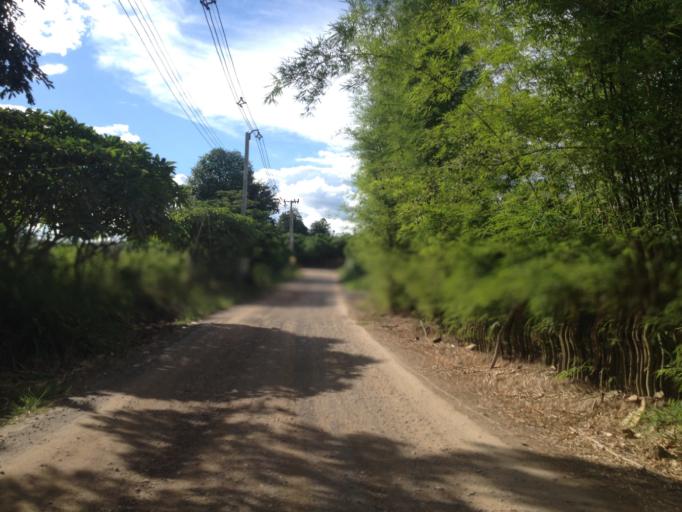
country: TH
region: Chiang Mai
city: Hang Dong
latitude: 18.7005
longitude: 98.8934
